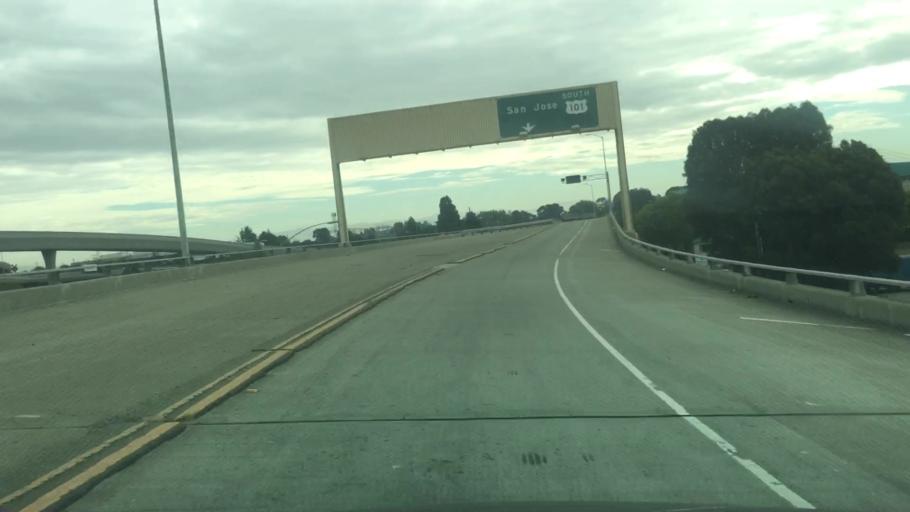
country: US
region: California
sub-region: San Mateo County
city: Foster City
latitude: 37.5524
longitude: -122.2982
